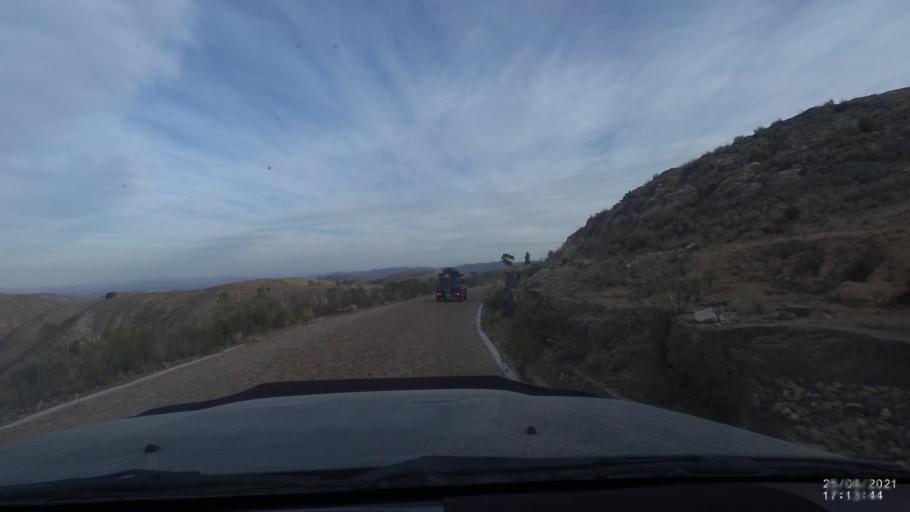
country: BO
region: Cochabamba
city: Arani
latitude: -17.8605
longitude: -65.6954
